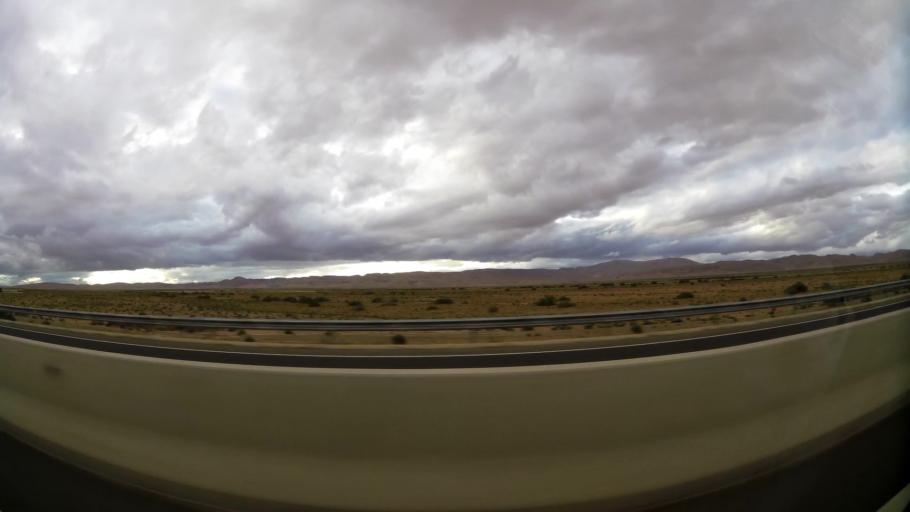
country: MA
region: Taza-Al Hoceima-Taounate
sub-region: Taza
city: Guercif
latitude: 34.3096
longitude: -3.6087
